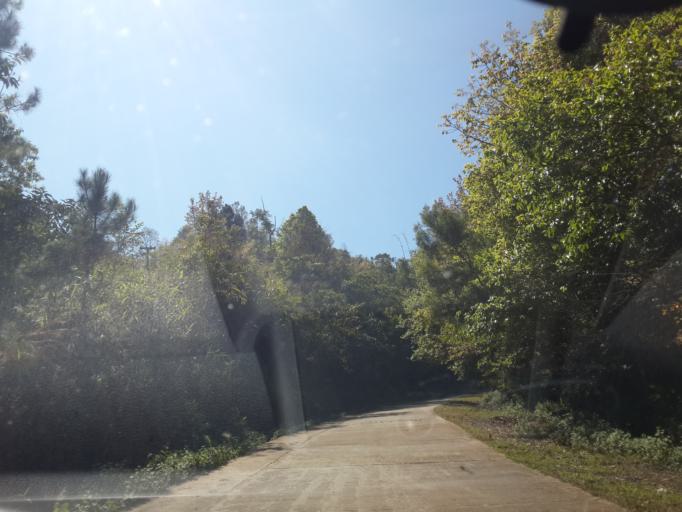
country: TH
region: Chiang Mai
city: Fang
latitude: 19.9200
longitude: 99.0499
